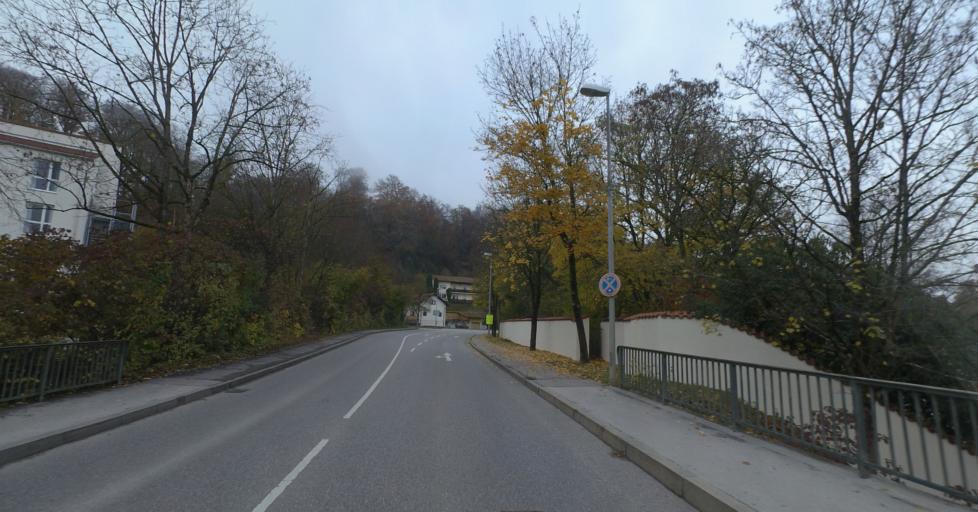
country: DE
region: Bavaria
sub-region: Upper Bavaria
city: Trostberg an der Alz
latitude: 48.0305
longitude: 12.5576
